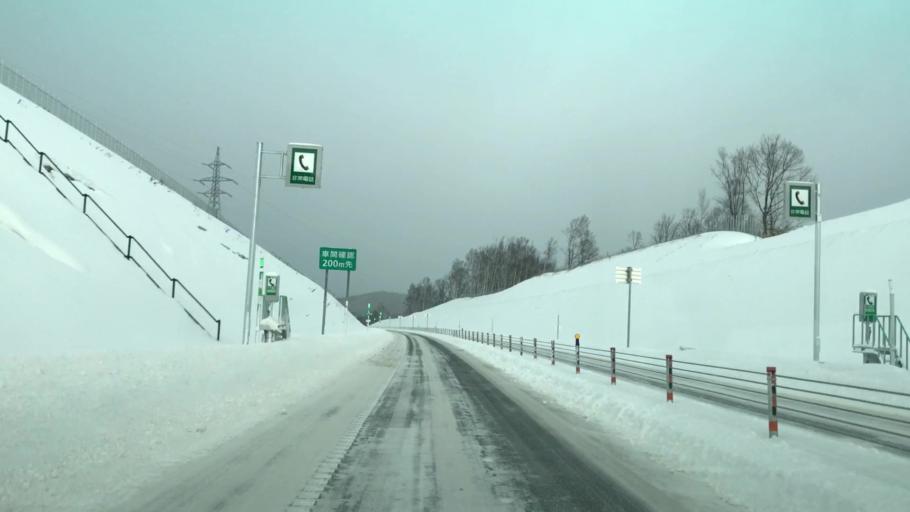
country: JP
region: Hokkaido
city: Otaru
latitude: 43.1901
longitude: 140.9577
